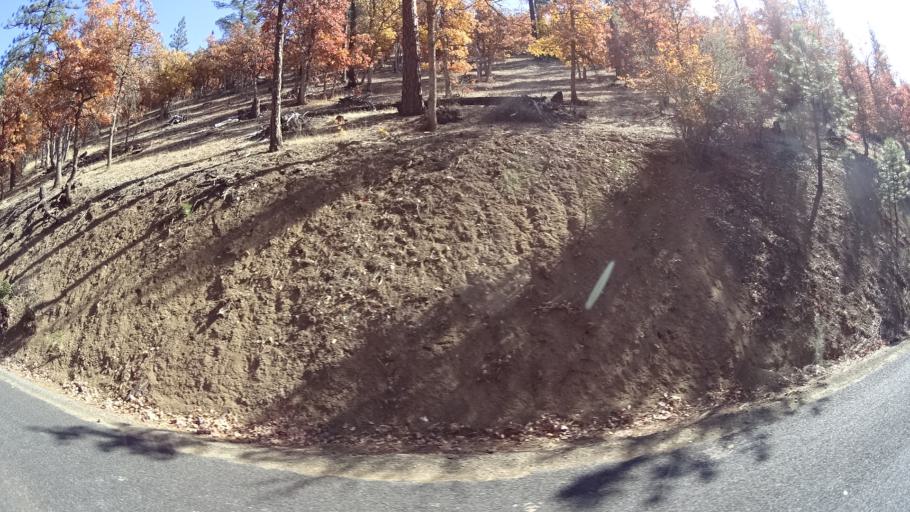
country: US
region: California
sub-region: Siskiyou County
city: Yreka
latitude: 41.6578
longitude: -122.8559
